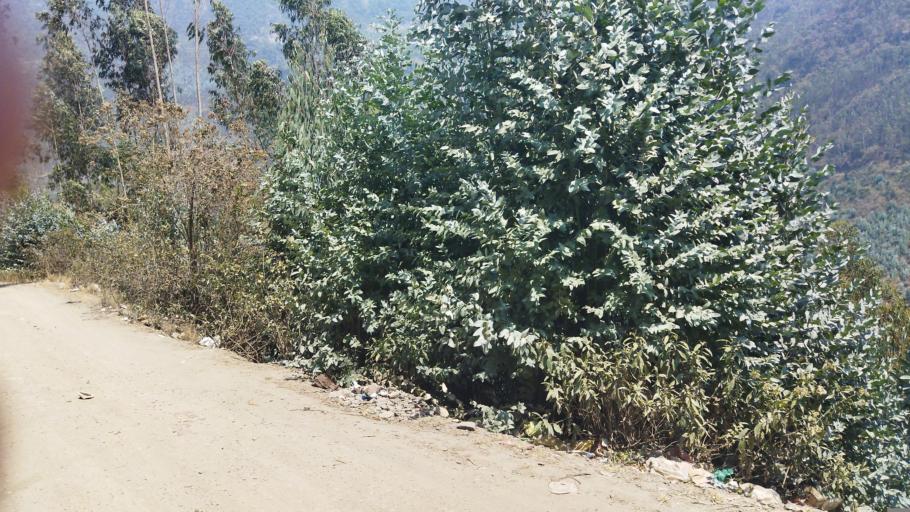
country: BO
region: La Paz
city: Quime
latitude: -16.9810
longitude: -67.2216
